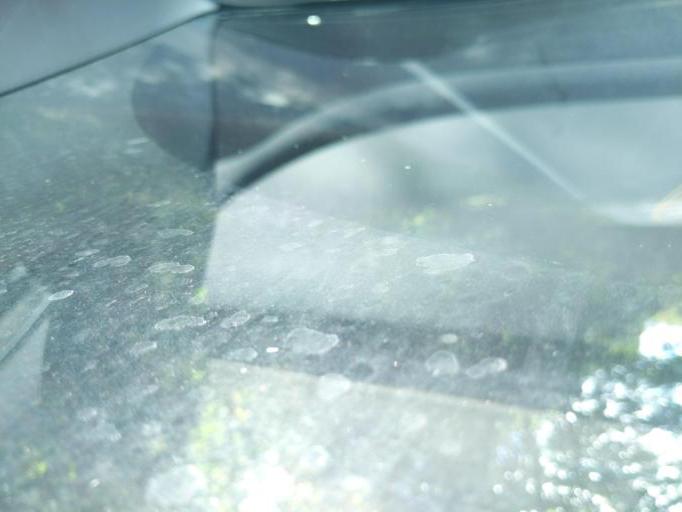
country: US
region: Michigan
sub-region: Antrim County
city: Bellaire
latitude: 44.9877
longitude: -85.2845
